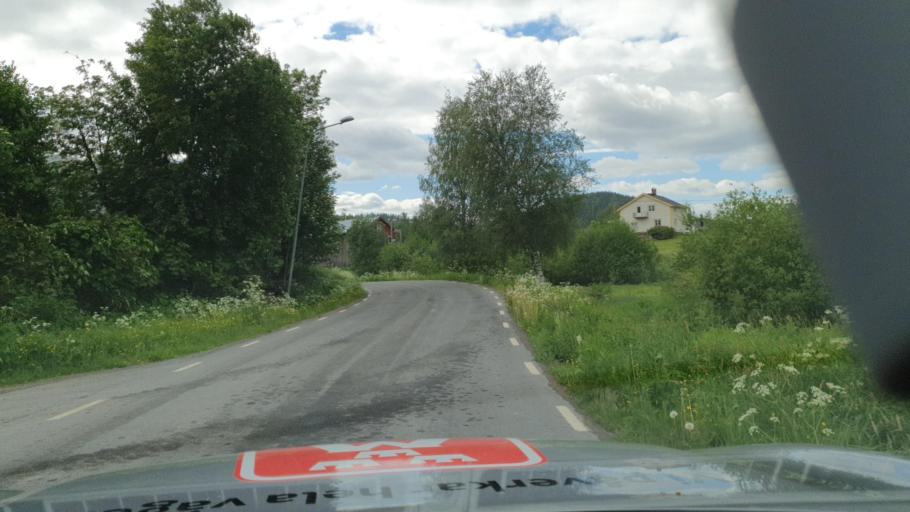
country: SE
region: Vaesternorrland
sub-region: Kramfors Kommun
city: Nordingra
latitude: 62.9095
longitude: 18.2994
